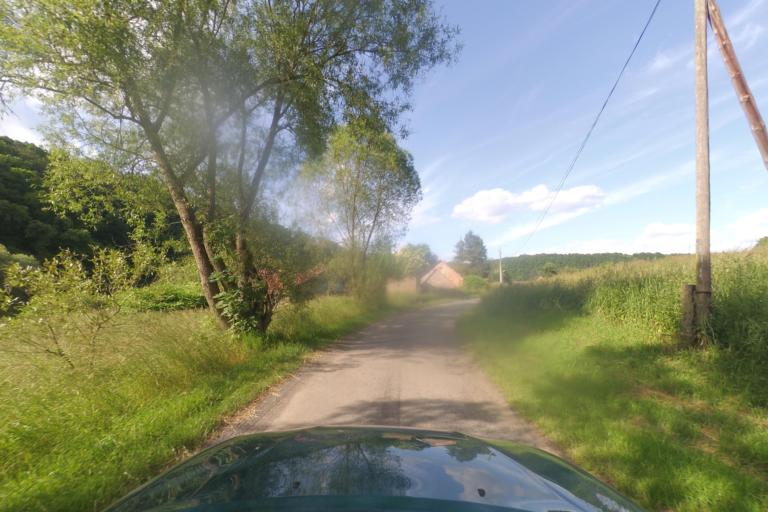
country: PL
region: Lower Silesian Voivodeship
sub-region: Powiat zabkowicki
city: Bardo
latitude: 50.4968
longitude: 16.6865
